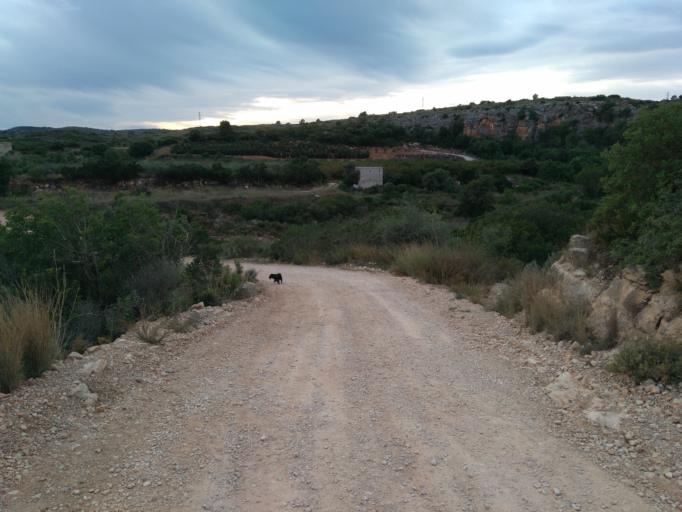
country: ES
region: Valencia
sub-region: Provincia de Valencia
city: Benimodo
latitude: 39.1987
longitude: -0.5860
